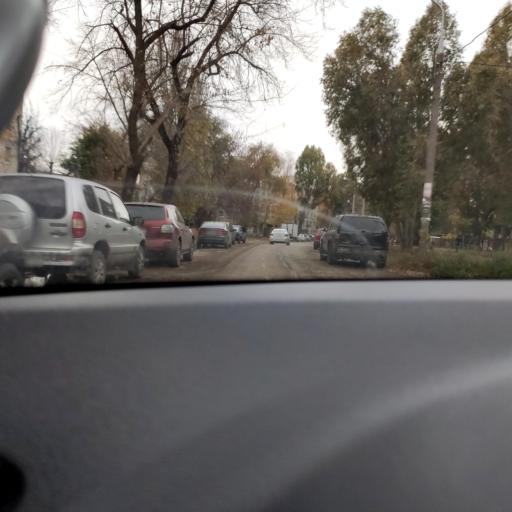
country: RU
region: Samara
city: Petra-Dubrava
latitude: 53.2320
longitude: 50.2801
